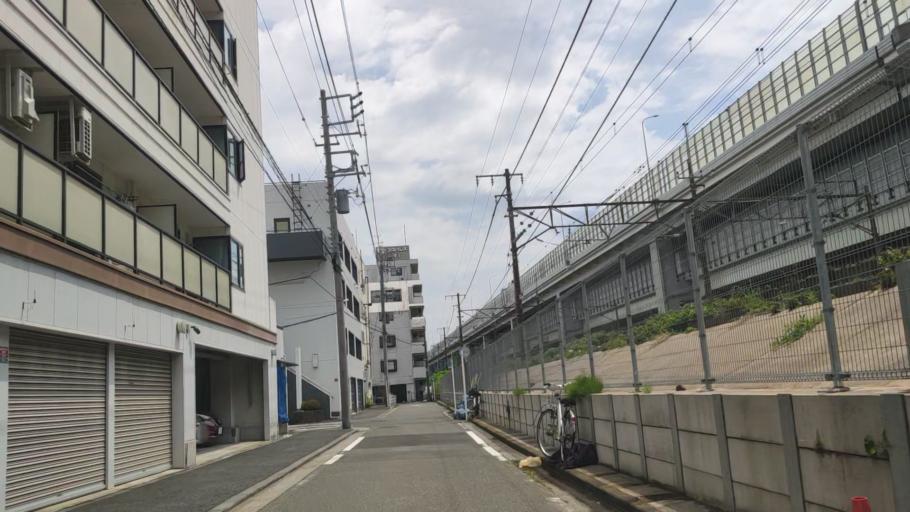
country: JP
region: Kanagawa
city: Yokohama
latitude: 35.4170
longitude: 139.6404
